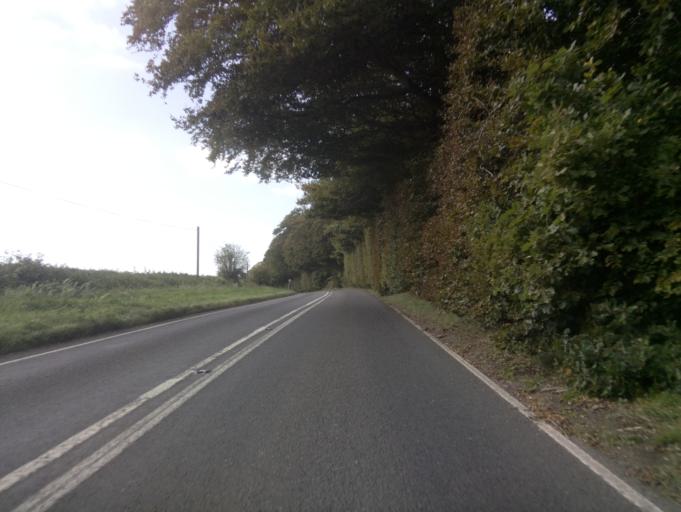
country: GB
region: England
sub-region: Hampshire
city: Basingstoke
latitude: 51.2324
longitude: -1.0724
